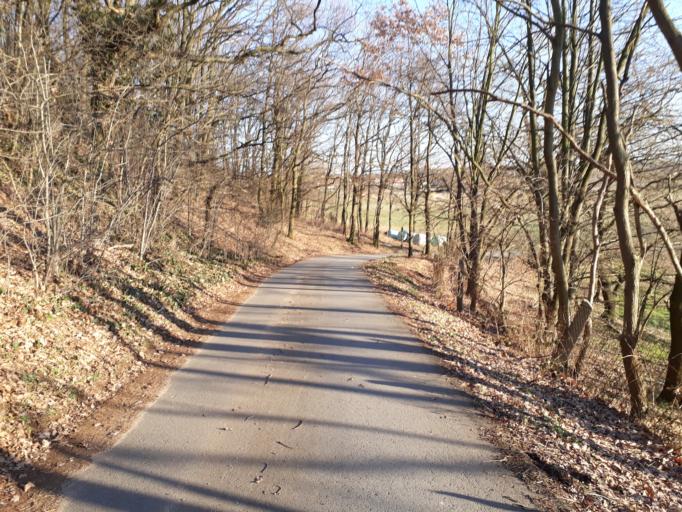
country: DE
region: Saxony
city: Heidenau
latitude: 51.0066
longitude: 13.8869
